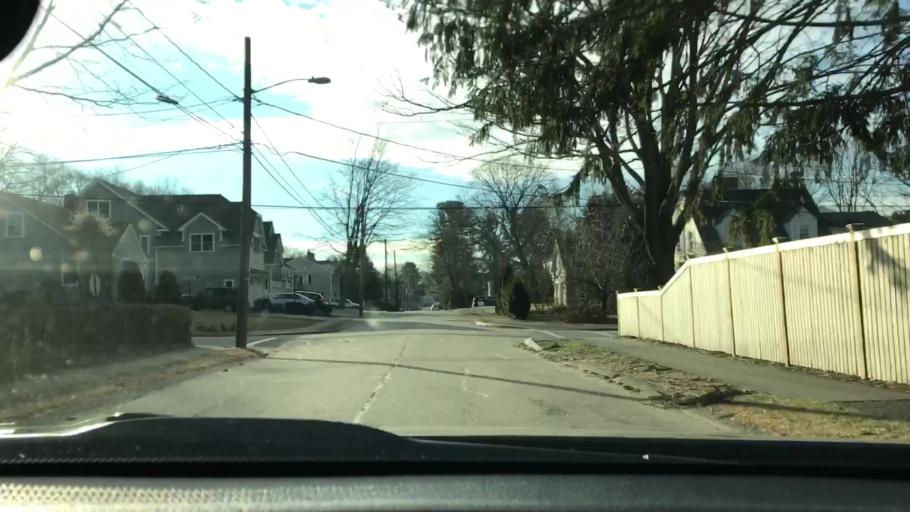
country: US
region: Massachusetts
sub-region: Norfolk County
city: Needham
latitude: 42.2914
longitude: -71.2292
